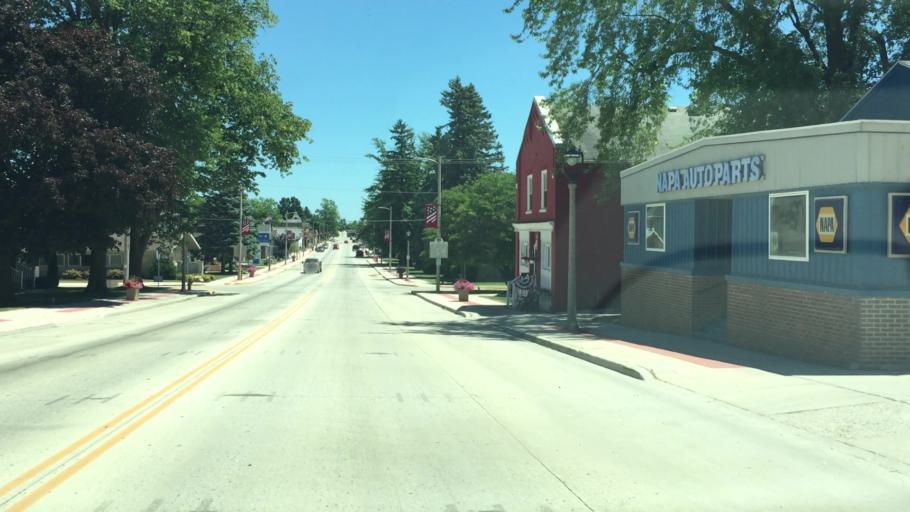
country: US
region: Wisconsin
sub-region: Calumet County
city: New Holstein
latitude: 43.9497
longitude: -88.0909
